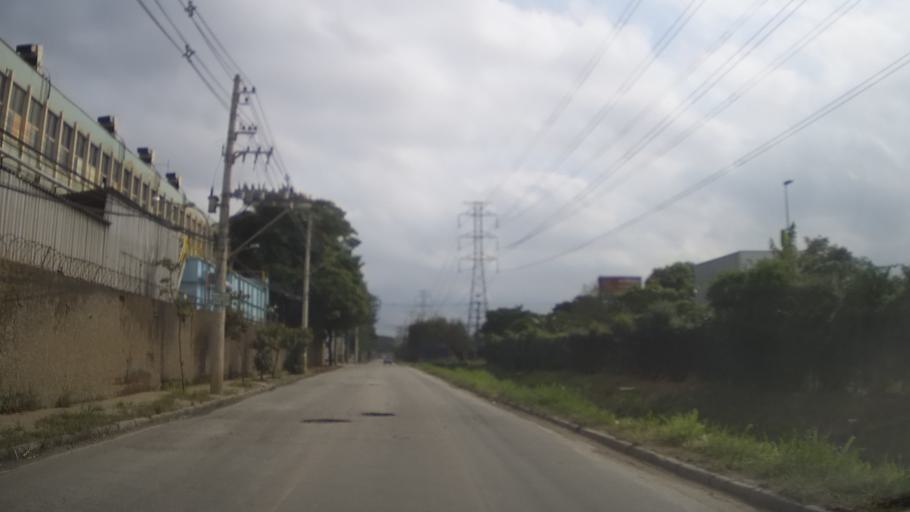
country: BR
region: Sao Paulo
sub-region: Guarulhos
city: Guarulhos
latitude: -23.4711
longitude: -46.4712
